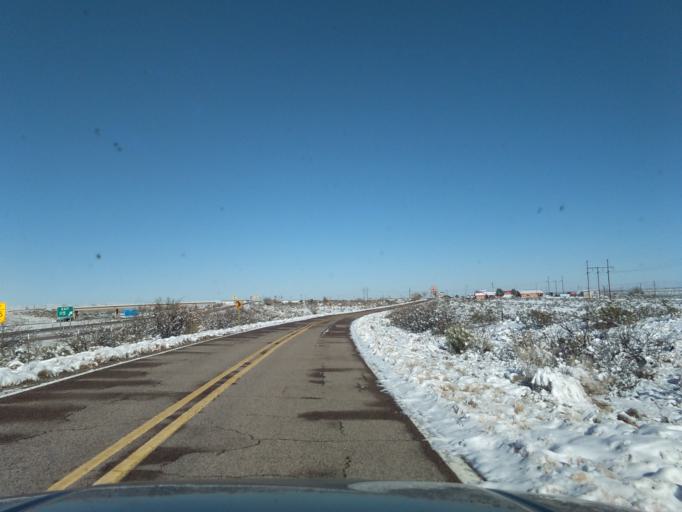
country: US
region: New Mexico
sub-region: Socorro County
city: Socorro
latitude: 33.6341
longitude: -107.1234
